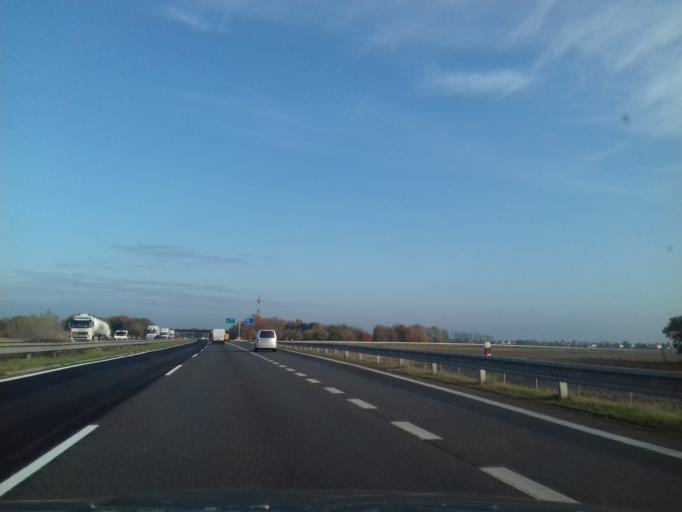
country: SK
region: Bratislavsky
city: Stupava
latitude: 48.3226
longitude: 17.0232
